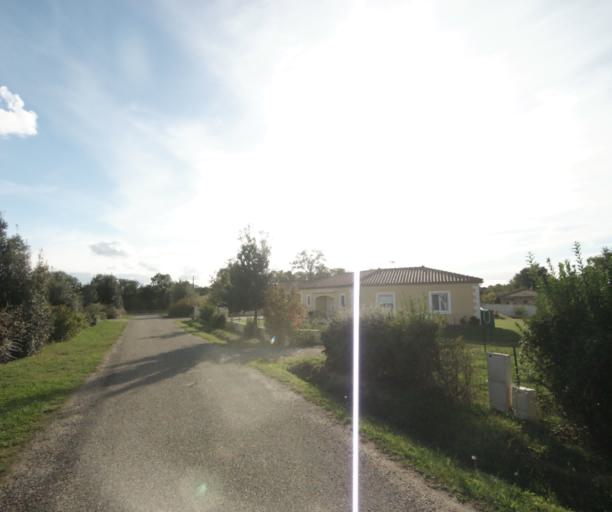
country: FR
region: Midi-Pyrenees
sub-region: Departement du Gers
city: Gondrin
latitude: 43.8910
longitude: 0.2370
